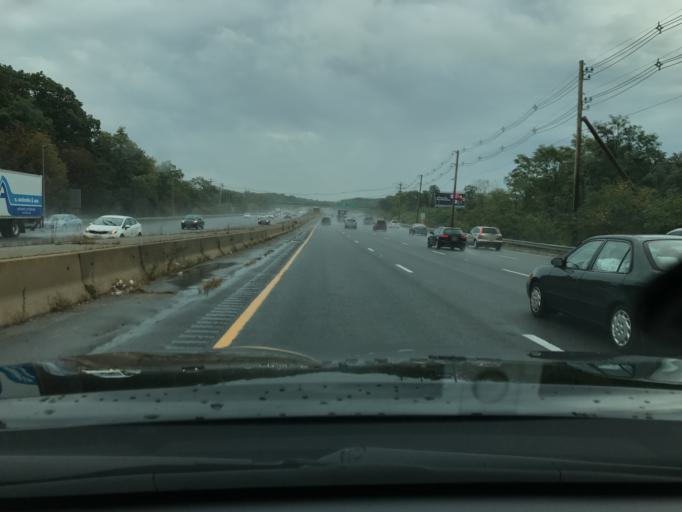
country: US
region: Massachusetts
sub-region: Essex County
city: South Peabody
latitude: 42.5217
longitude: -70.9875
